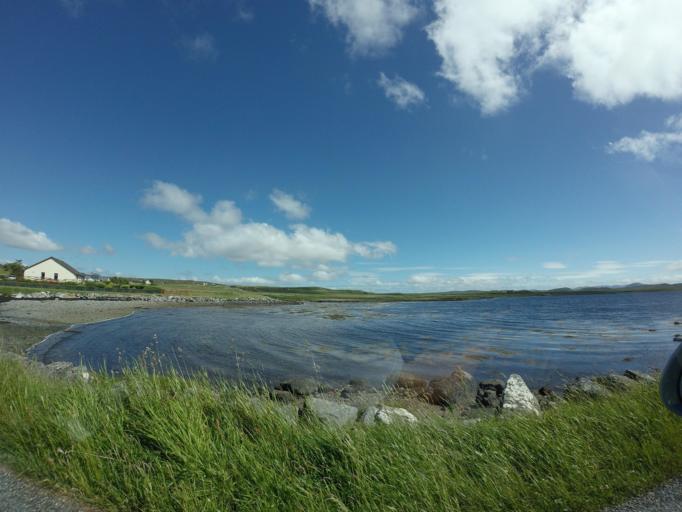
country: GB
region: Scotland
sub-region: Eilean Siar
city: Harris
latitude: 58.1971
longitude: -6.7412
